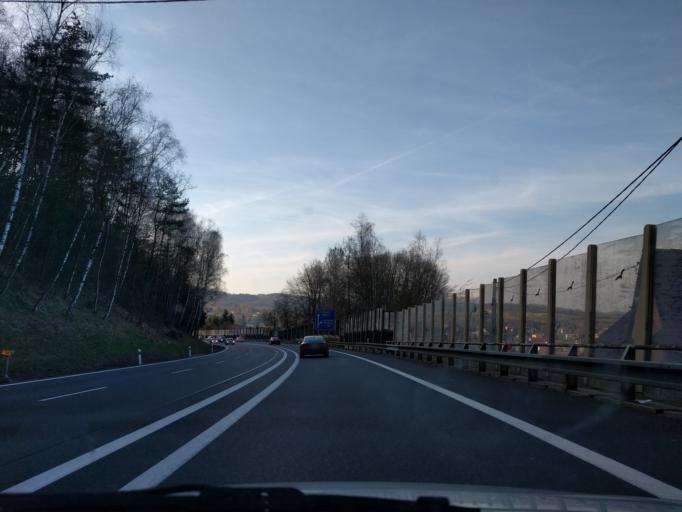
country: CZ
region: Central Bohemia
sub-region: Okres Praha-Vychod
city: Mnichovice
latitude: 49.9045
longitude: 14.7149
